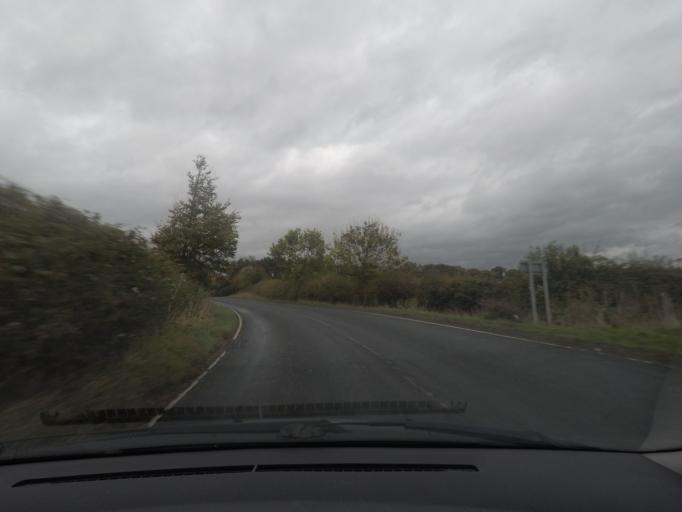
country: GB
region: England
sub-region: City of York
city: Wigginton
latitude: 54.0954
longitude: -1.1101
